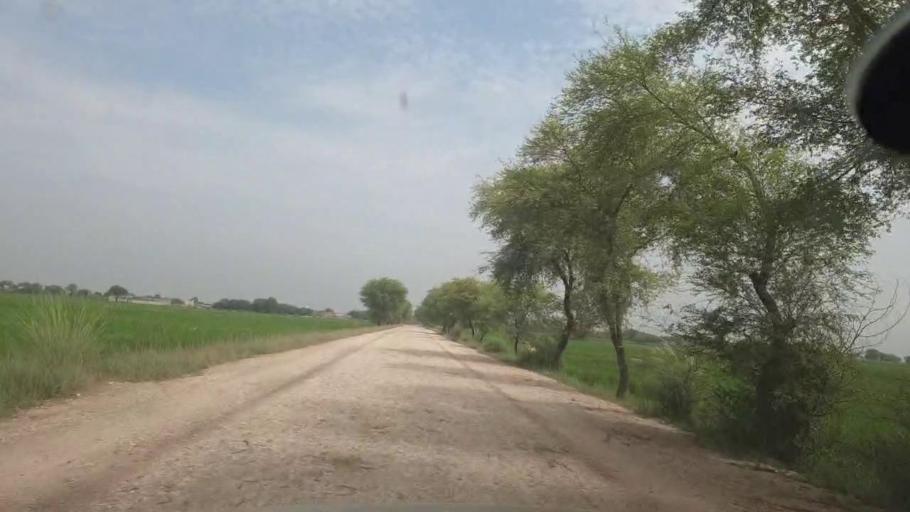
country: PK
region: Sindh
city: Jacobabad
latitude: 28.2479
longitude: 68.5421
